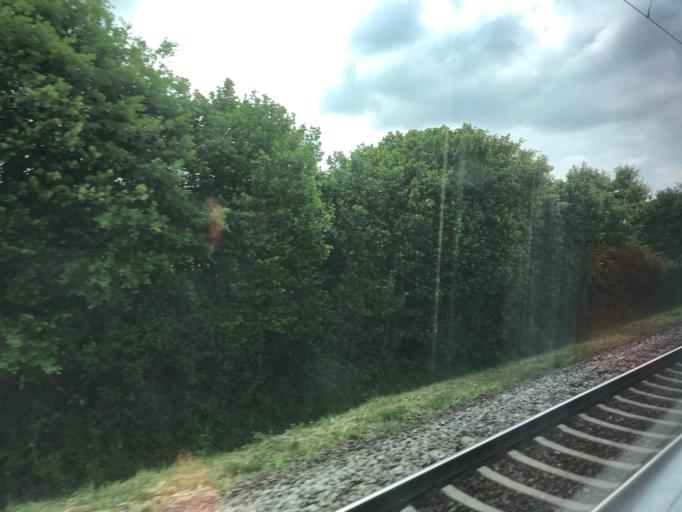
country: DE
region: Baden-Wuerttemberg
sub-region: Tuebingen Region
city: Westerstetten
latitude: 48.5081
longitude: 9.9502
